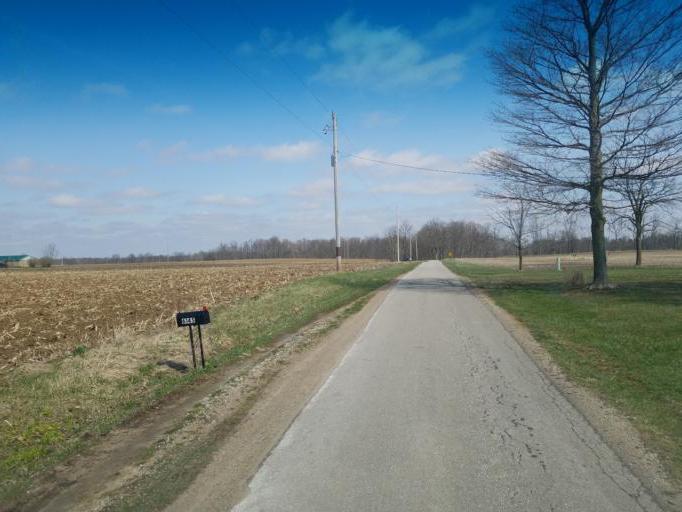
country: US
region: Ohio
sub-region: Crawford County
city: Bucyrus
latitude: 40.9264
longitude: -83.0598
